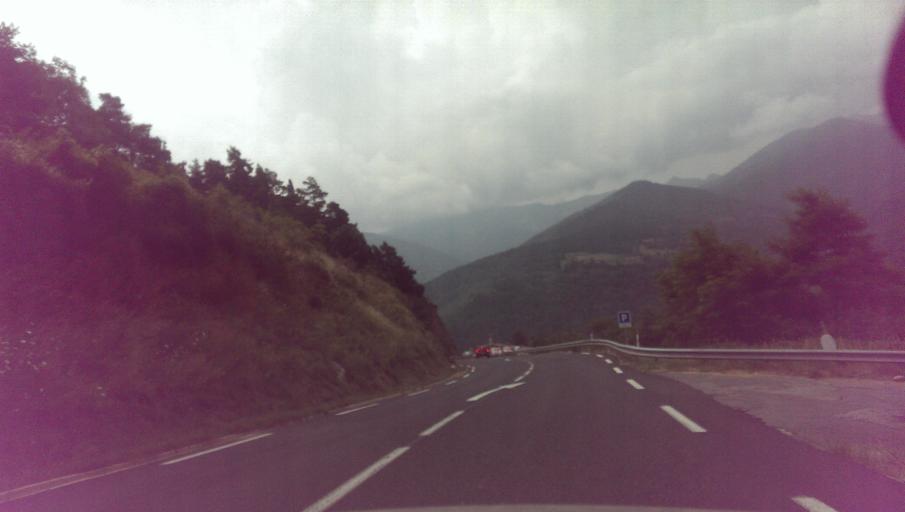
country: ES
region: Catalonia
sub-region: Provincia de Girona
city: Llivia
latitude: 42.5076
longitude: 2.1430
